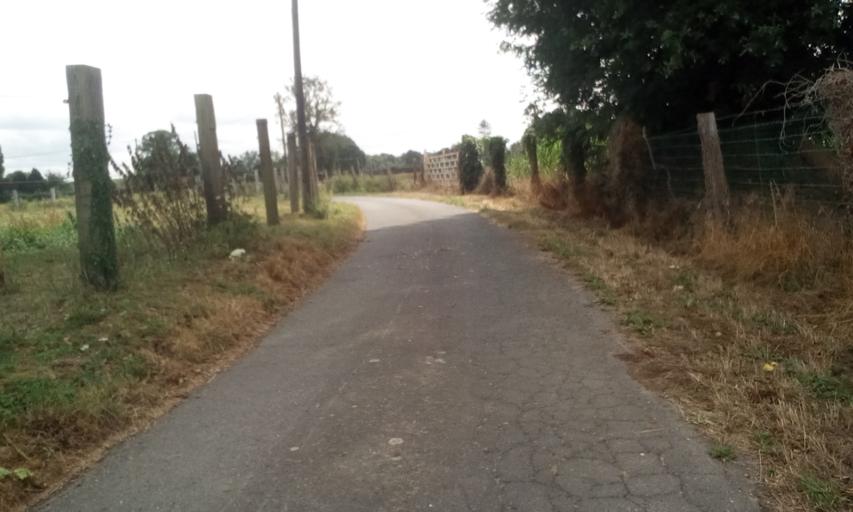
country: FR
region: Lower Normandy
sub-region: Departement du Calvados
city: Merville-Franceville-Plage
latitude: 49.2517
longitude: -0.1941
